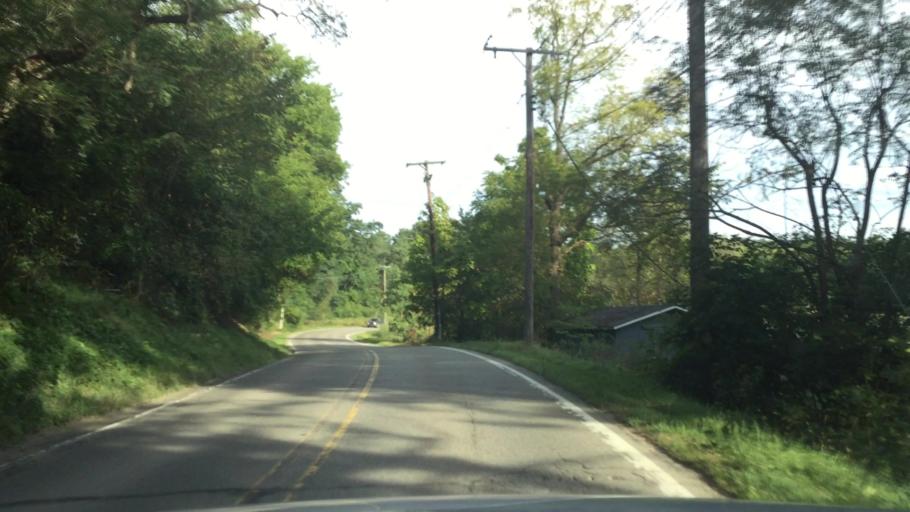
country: US
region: Michigan
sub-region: Livingston County
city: Brighton
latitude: 42.4738
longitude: -83.8344
